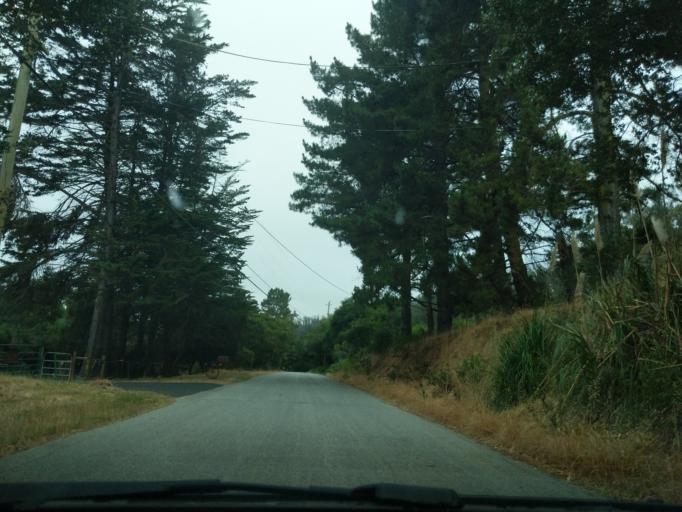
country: US
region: California
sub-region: San Benito County
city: Aromas
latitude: 36.8860
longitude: -121.6188
